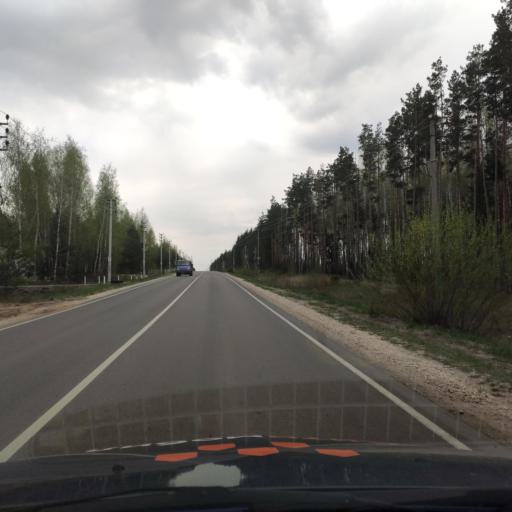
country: RU
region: Voronezj
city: Podgornoye
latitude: 51.8653
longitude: 39.1703
